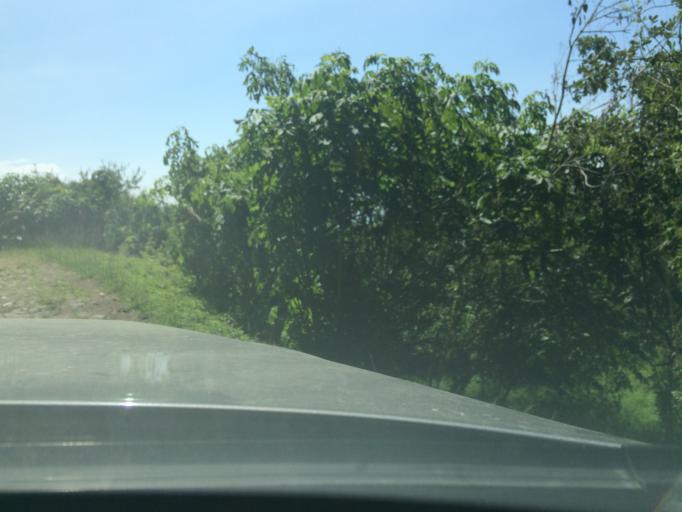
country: MX
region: Colima
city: Suchitlan
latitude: 19.4129
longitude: -103.6754
